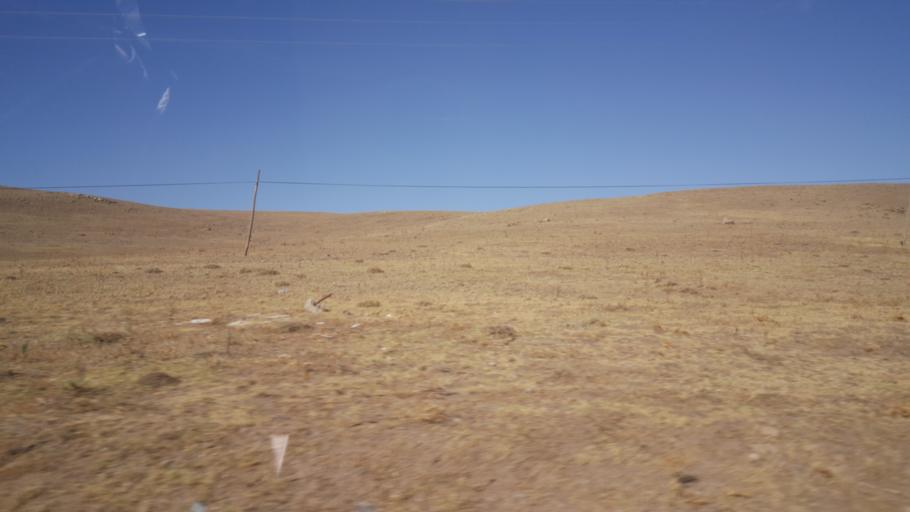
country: TR
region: Ankara
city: Altpinar
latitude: 39.1701
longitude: 32.7025
